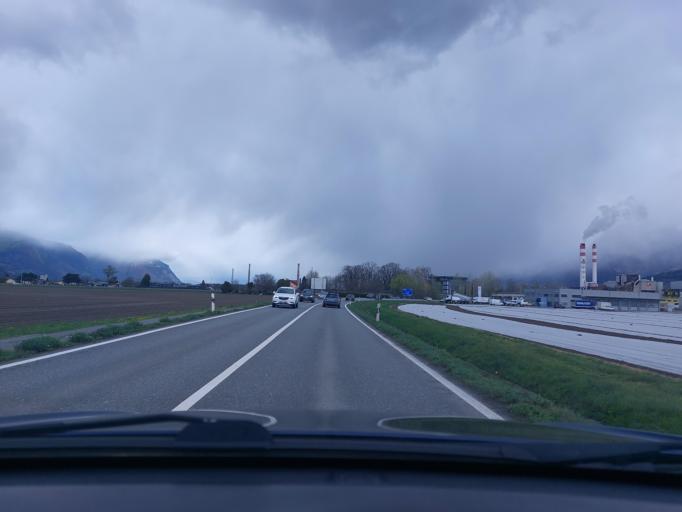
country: CH
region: Valais
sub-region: Monthey District
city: Collombey
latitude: 46.2713
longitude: 6.9580
